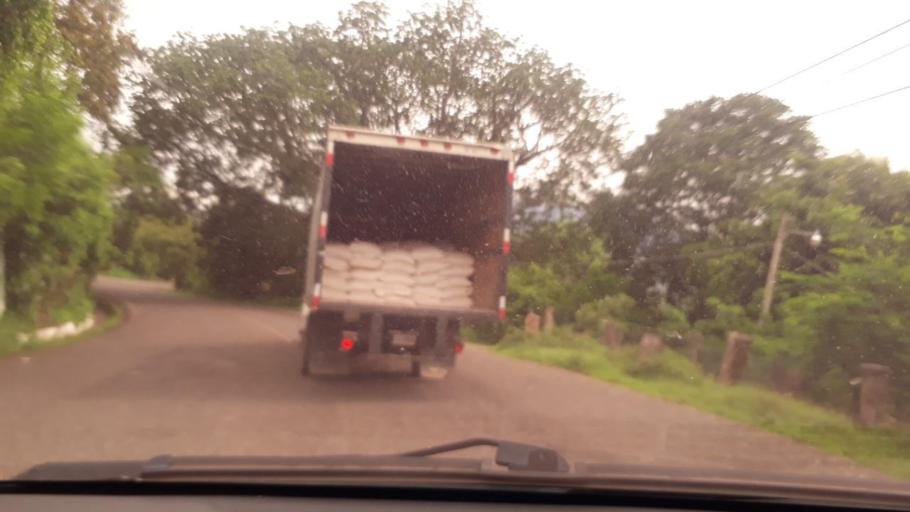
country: GT
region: Jutiapa
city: Santa Catarina Mita
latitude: 14.4705
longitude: -89.7152
